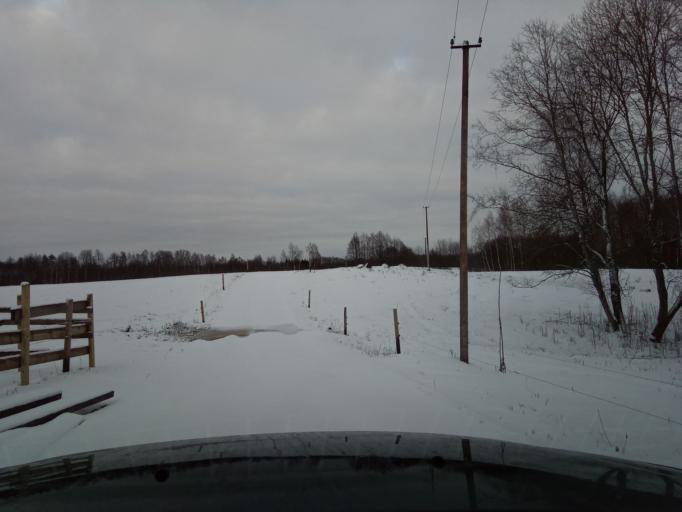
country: LT
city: Zarasai
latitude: 55.7308
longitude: 25.9572
